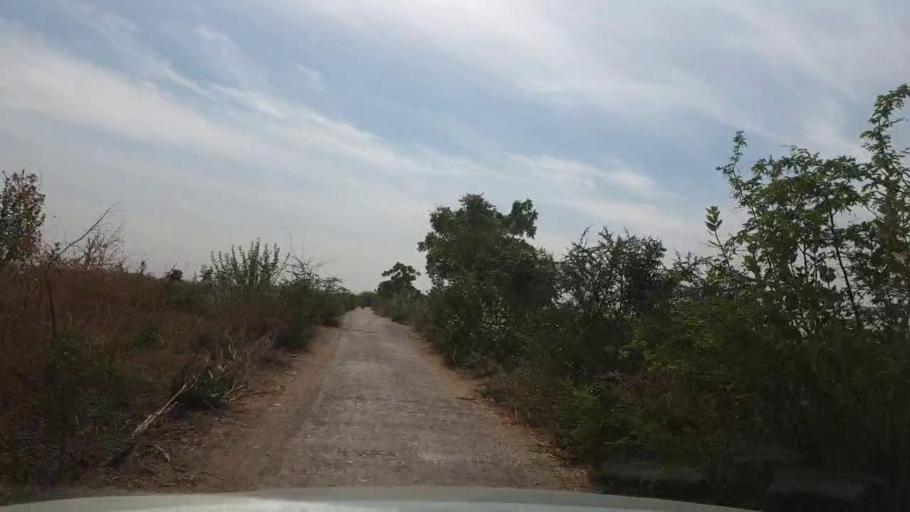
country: PK
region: Sindh
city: Nabisar
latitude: 25.0858
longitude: 69.5998
